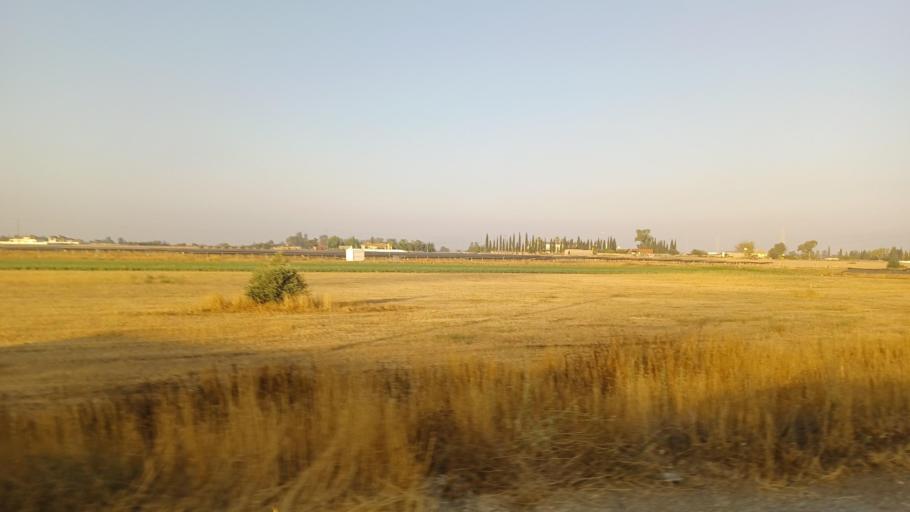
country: CY
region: Ammochostos
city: Avgorou
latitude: 35.0326
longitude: 33.8556
